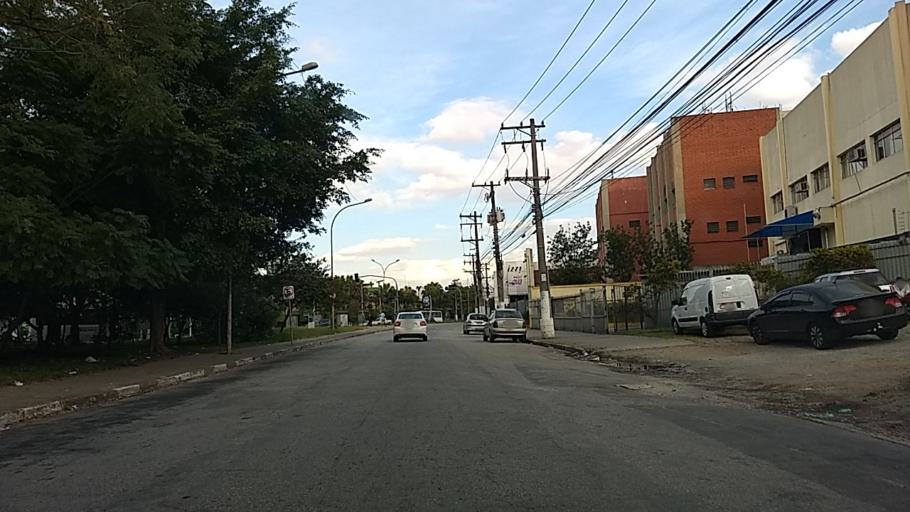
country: BR
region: Sao Paulo
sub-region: Sao Paulo
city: Sao Paulo
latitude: -23.5108
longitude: -46.7061
